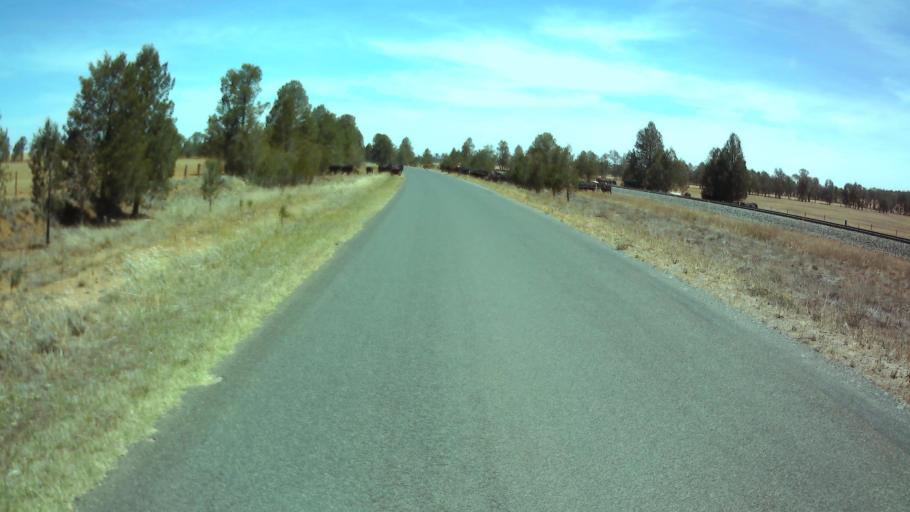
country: AU
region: New South Wales
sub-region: Weddin
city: Grenfell
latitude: -33.7777
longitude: 147.7541
